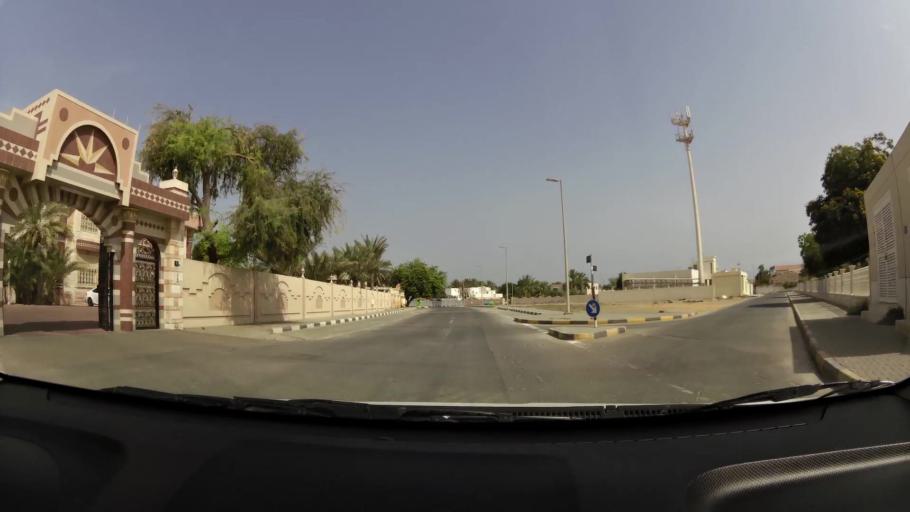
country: AE
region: Ash Shariqah
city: Sharjah
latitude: 25.3512
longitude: 55.4175
